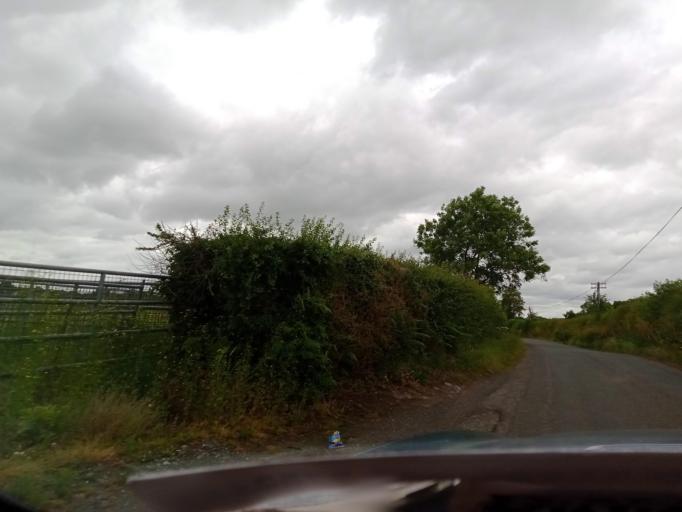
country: IE
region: Leinster
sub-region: Kilkenny
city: Thomastown
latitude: 52.5660
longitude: -7.1977
